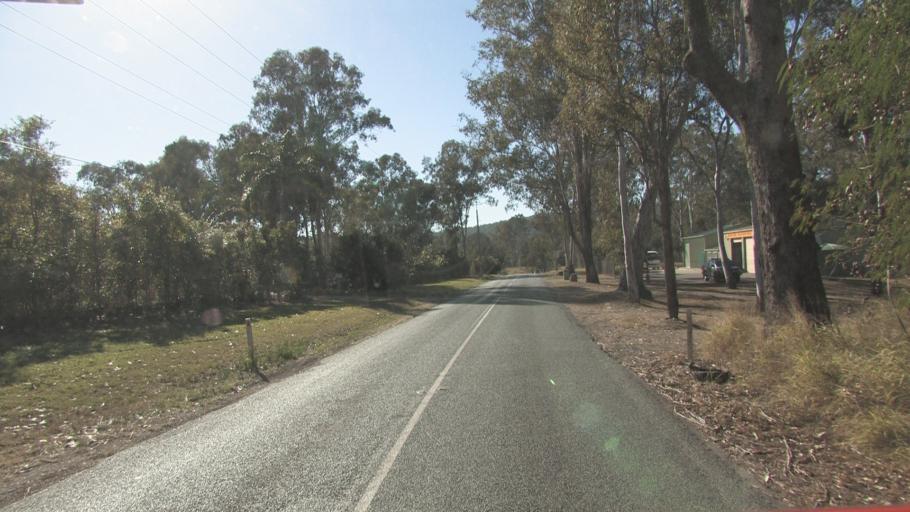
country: AU
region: Queensland
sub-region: Logan
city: Windaroo
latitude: -27.7965
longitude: 153.1748
